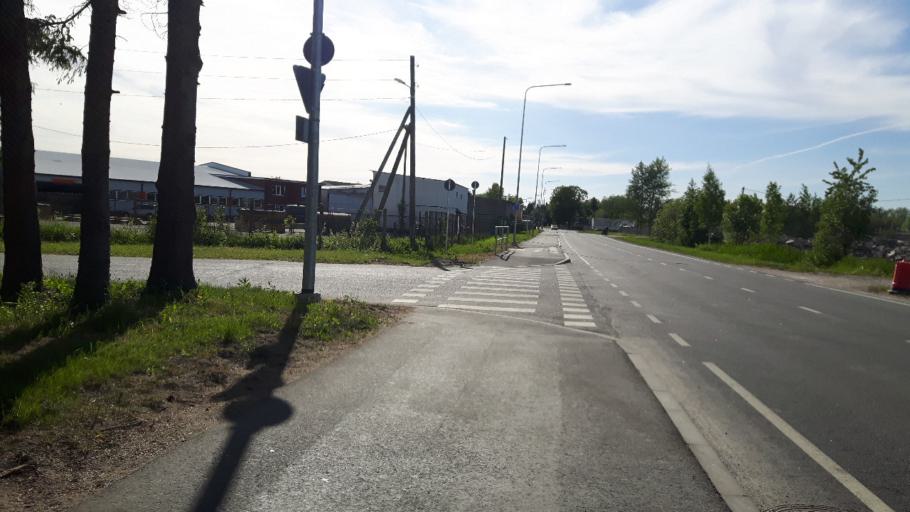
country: EE
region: Harju
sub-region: Joelaehtme vald
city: Loo
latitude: 59.4311
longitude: 24.9591
